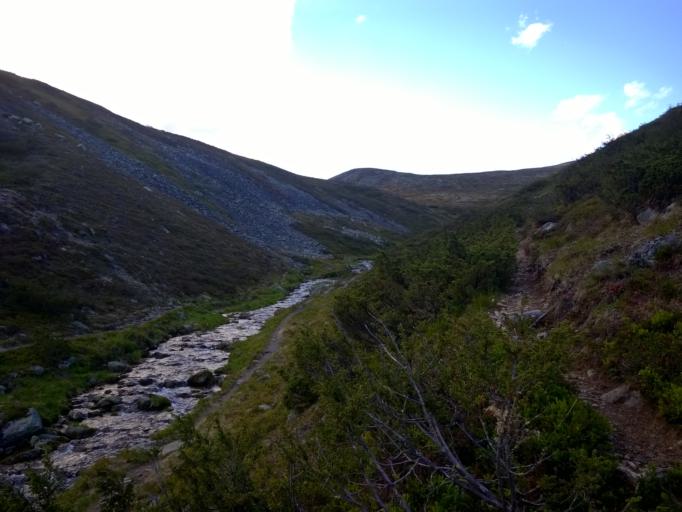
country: FI
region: Lapland
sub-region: Tunturi-Lappi
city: Muonio
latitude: 68.0621
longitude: 24.0529
